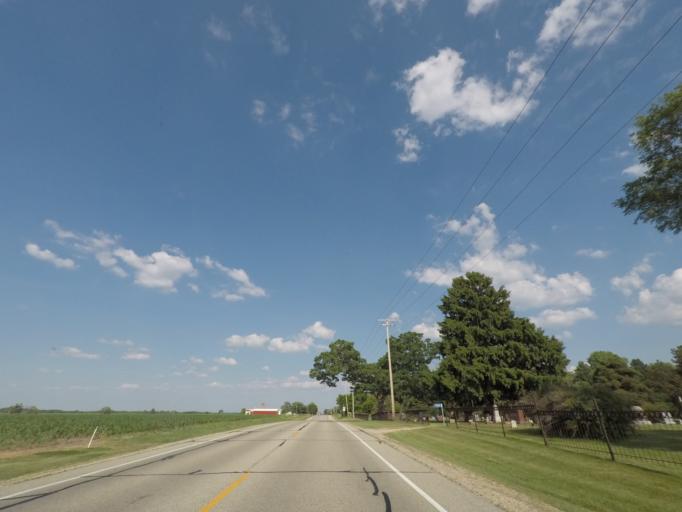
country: US
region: Wisconsin
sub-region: Walworth County
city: East Troy
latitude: 42.7929
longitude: -88.4697
